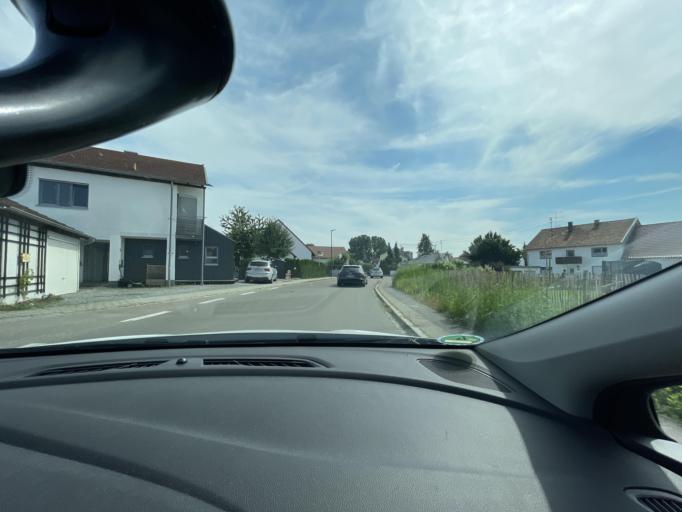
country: DE
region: Bavaria
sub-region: Upper Bavaria
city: Rohrmoos
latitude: 48.3216
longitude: 11.4131
